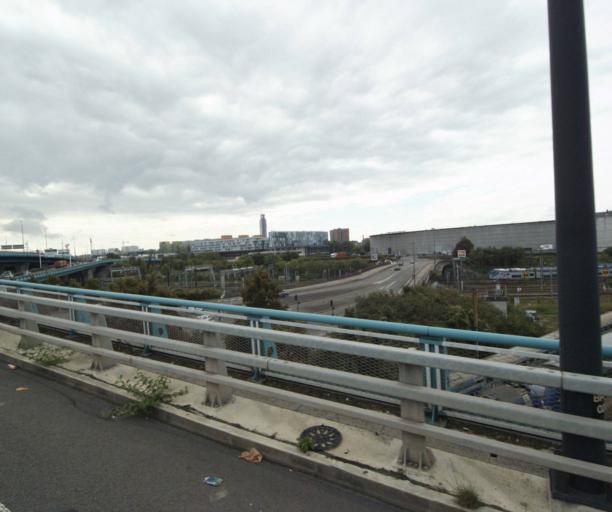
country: FR
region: Nord-Pas-de-Calais
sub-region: Departement du Nord
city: La Madeleine
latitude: 50.6339
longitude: 3.0820
